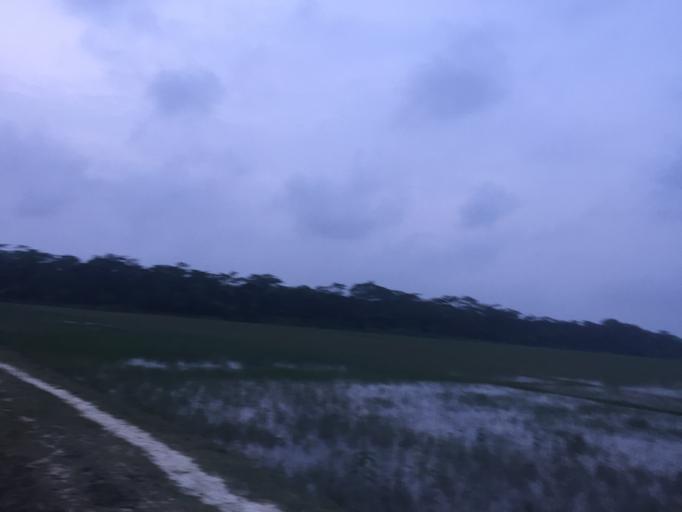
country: BD
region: Barisal
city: Mathba
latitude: 22.1933
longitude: 89.9339
